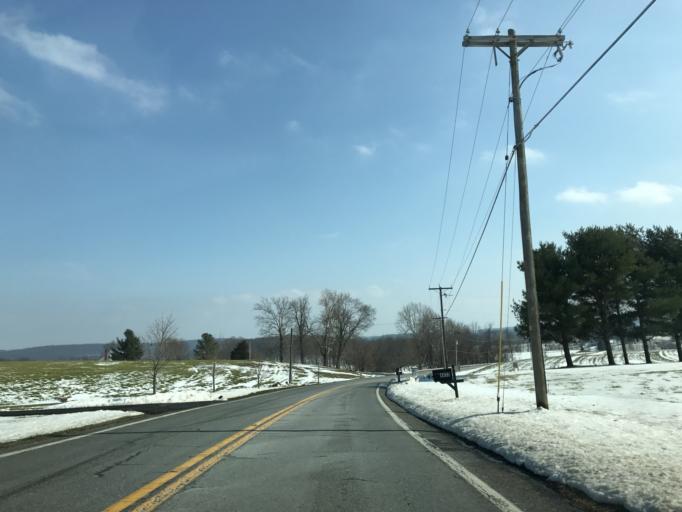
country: US
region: Pennsylvania
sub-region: York County
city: Susquehanna Trails
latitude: 39.7157
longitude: -76.3895
